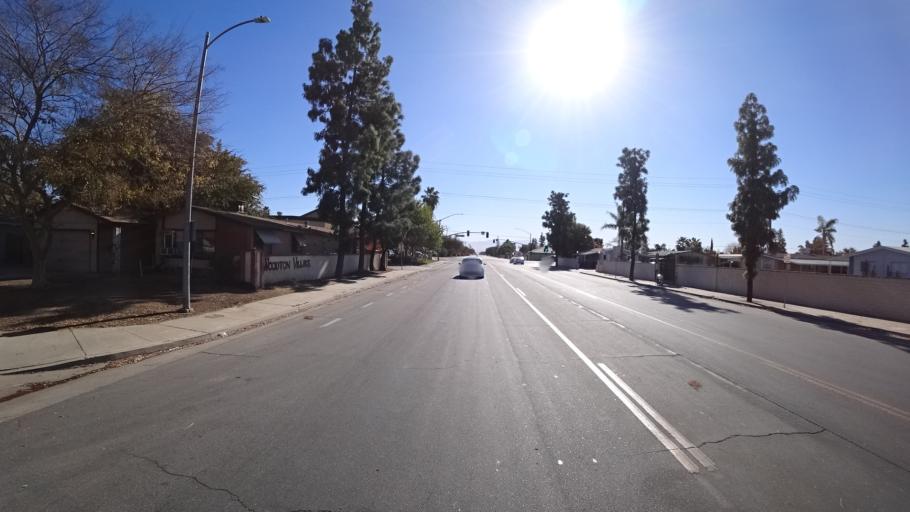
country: US
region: California
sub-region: Kern County
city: Greenfield
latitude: 35.2968
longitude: -119.0478
